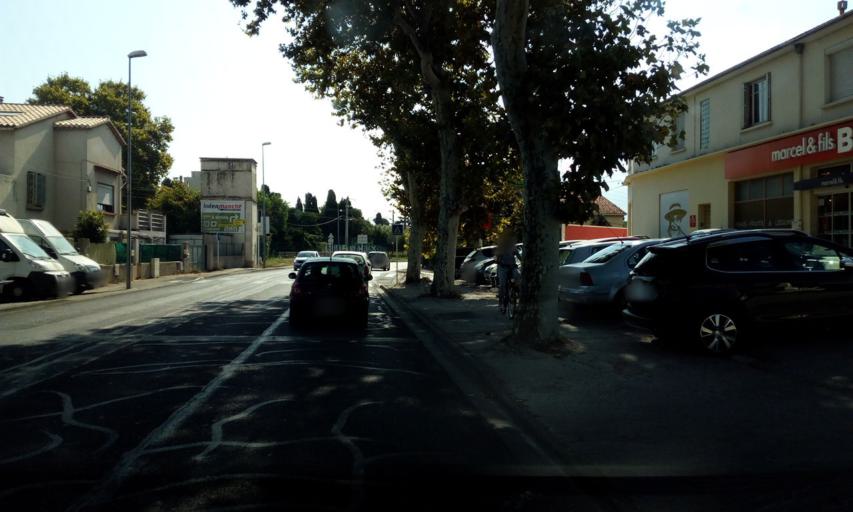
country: FR
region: Provence-Alpes-Cote d'Azur
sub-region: Departement du Var
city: La Valette-du-Var
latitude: 43.1189
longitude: 5.9795
